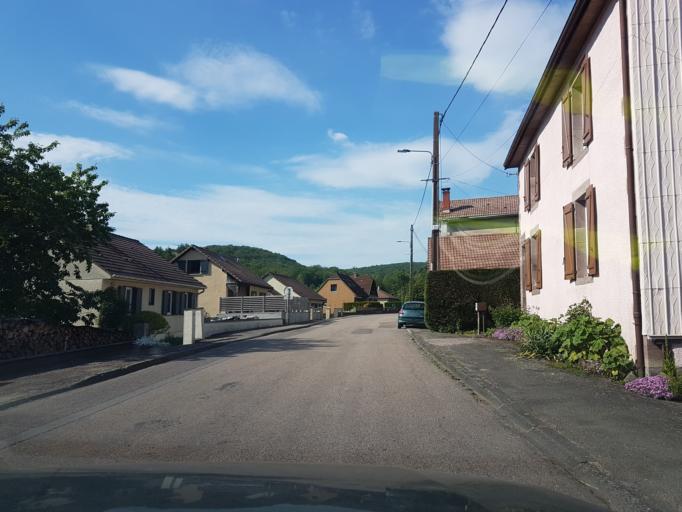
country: FR
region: Franche-Comte
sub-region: Departement de la Haute-Saone
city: Froideconche
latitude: 47.8463
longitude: 6.4749
